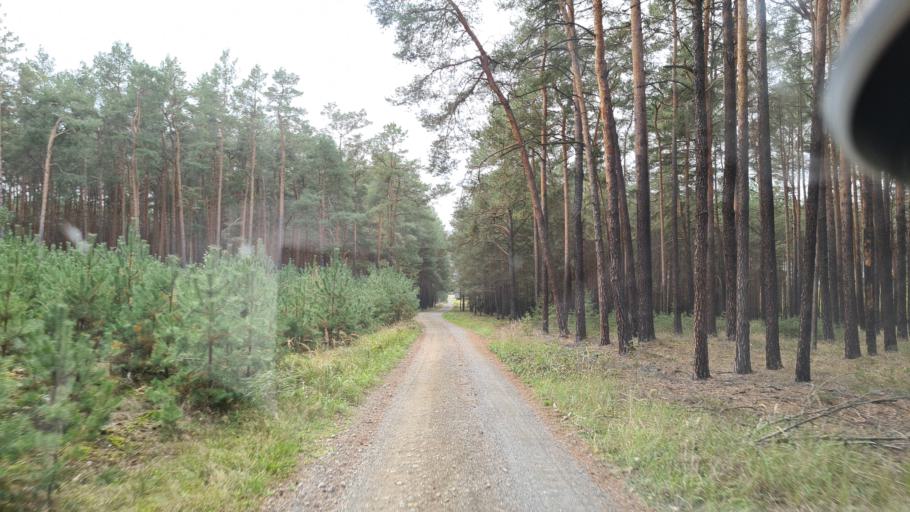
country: DE
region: Brandenburg
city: Schonewalde
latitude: 51.7061
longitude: 13.5760
